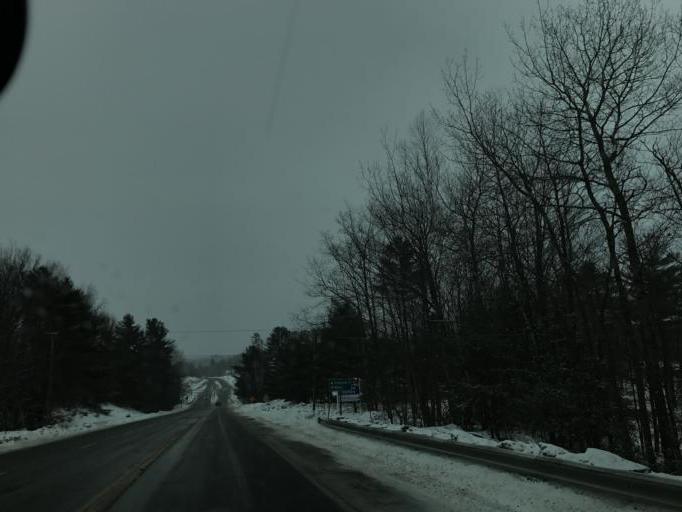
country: US
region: Maine
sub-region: Franklin County
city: Wilton
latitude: 44.5844
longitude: -70.2134
